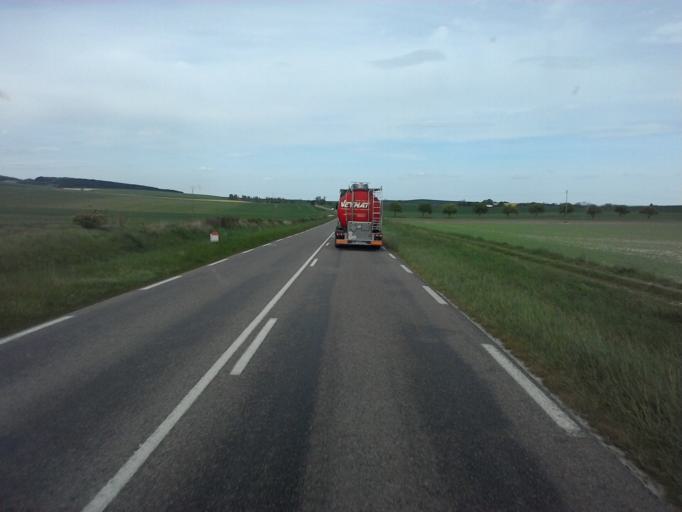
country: FR
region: Champagne-Ardenne
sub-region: Departement de l'Aube
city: Bouilly
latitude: 48.1375
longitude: 3.9993
